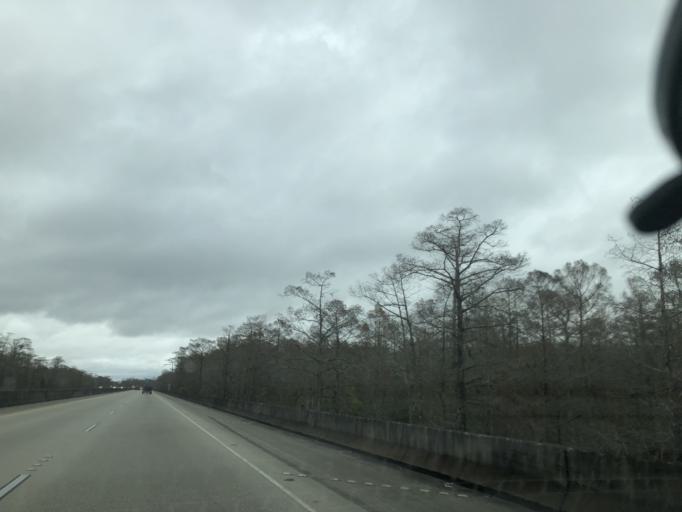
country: US
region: Louisiana
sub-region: Saint Charles Parish
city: Destrehan
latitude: 29.9646
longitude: -90.3472
